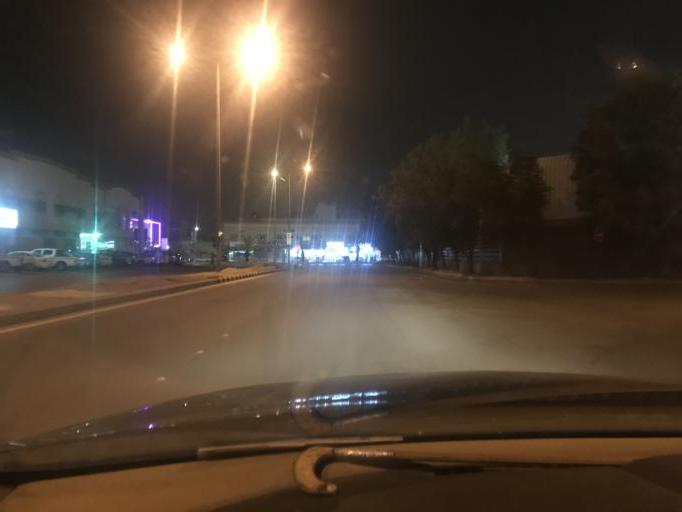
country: SA
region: Ar Riyad
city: Riyadh
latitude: 24.7509
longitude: 46.7789
